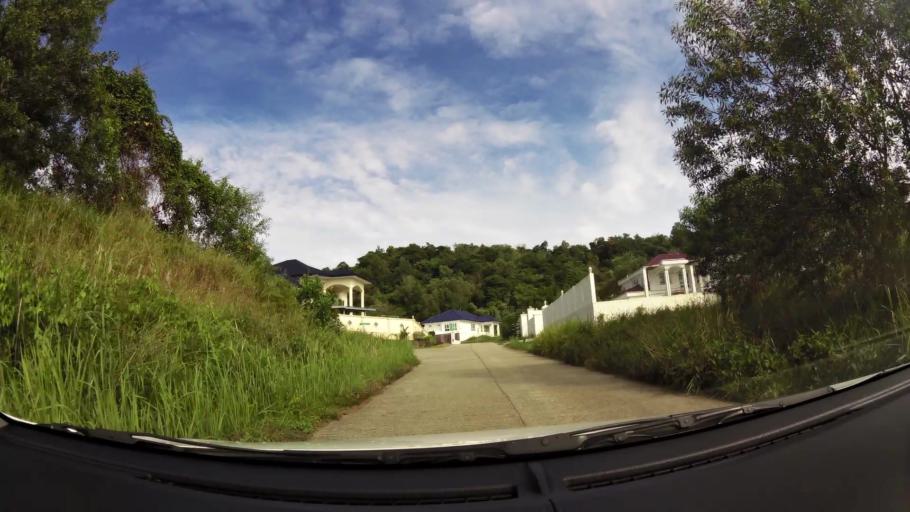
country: BN
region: Brunei and Muara
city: Bandar Seri Begawan
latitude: 4.8981
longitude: 114.9647
